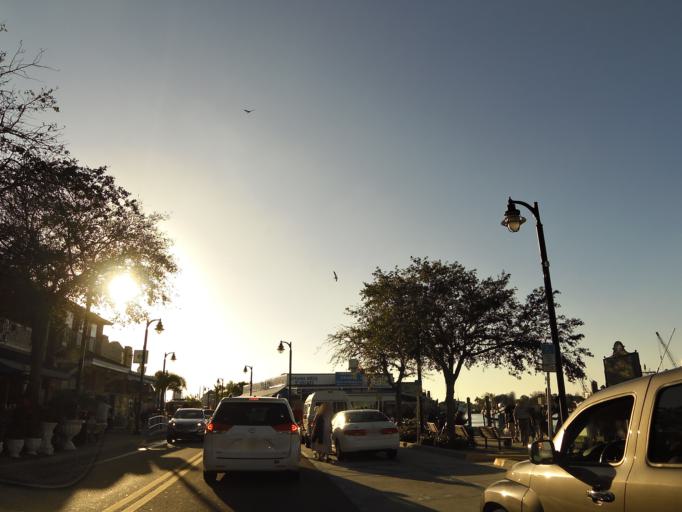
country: US
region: Florida
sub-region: Pinellas County
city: Tarpon Springs
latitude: 28.1556
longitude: -82.7611
